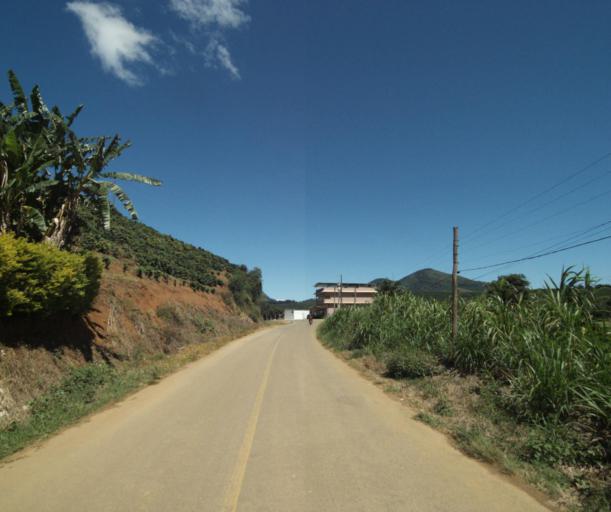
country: BR
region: Minas Gerais
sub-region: Espera Feliz
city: Espera Feliz
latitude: -20.5645
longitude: -41.8272
